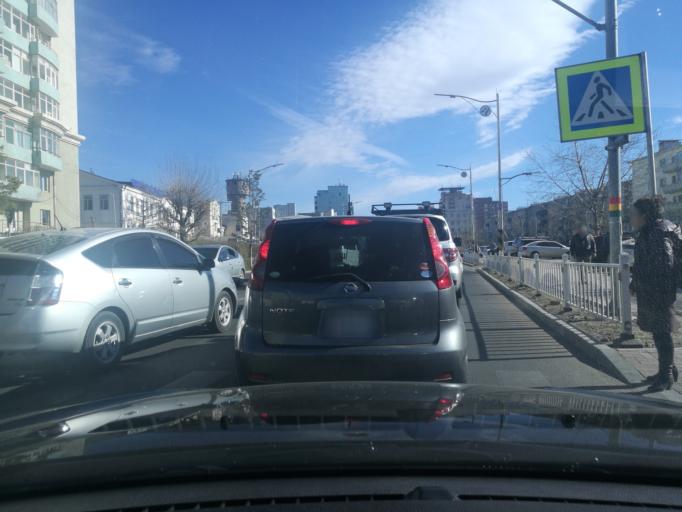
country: MN
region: Ulaanbaatar
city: Ulaanbaatar
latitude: 47.9133
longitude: 106.8949
